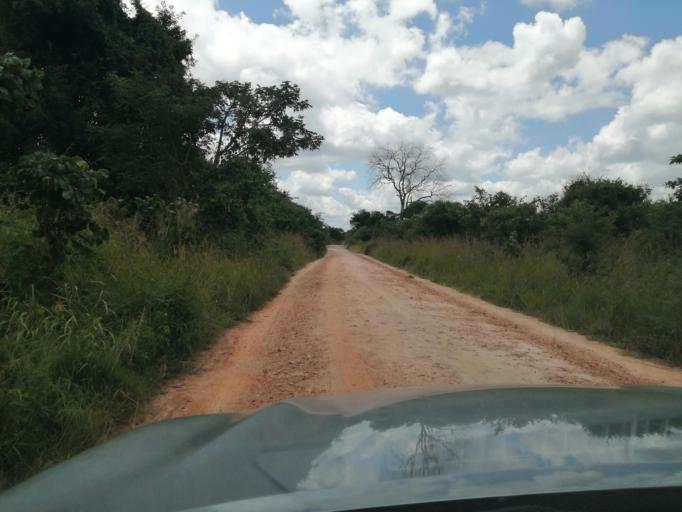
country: ZM
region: Lusaka
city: Lusaka
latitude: -15.1323
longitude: 27.9097
